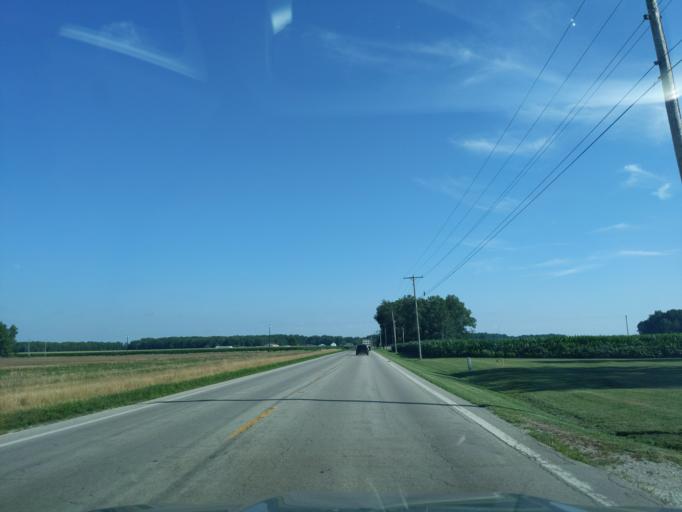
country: US
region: Indiana
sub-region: Ripley County
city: Osgood
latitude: 39.1640
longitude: -85.3087
